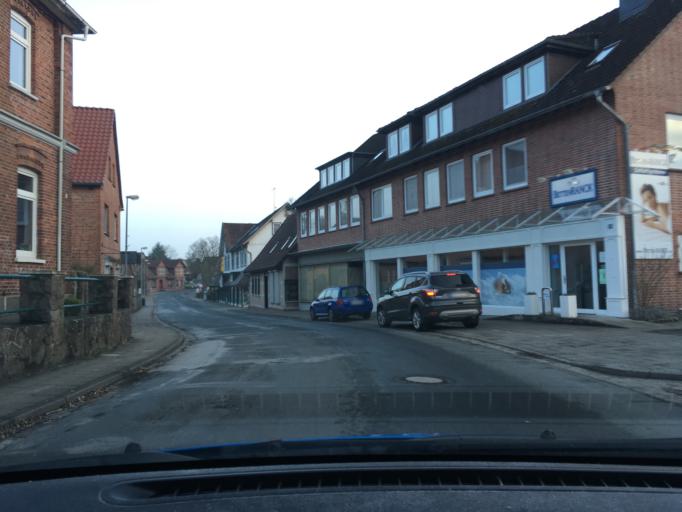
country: DE
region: Lower Saxony
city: Bad Fallingbostel
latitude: 52.9032
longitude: 9.7697
